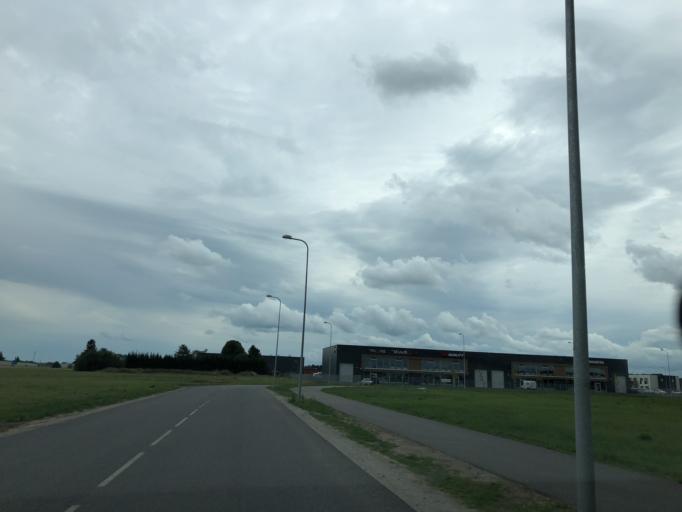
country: EE
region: Harju
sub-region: Rae vald
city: Jueri
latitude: 59.3902
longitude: 24.8240
